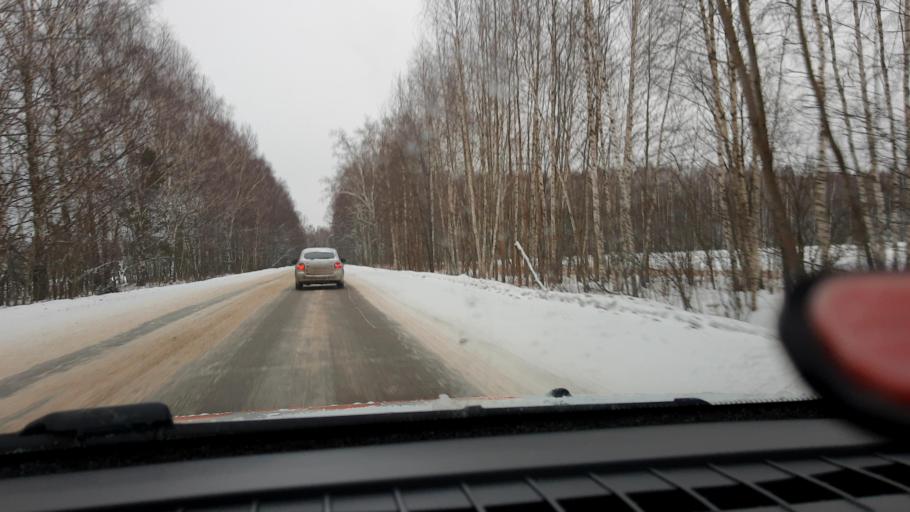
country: RU
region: Nizjnij Novgorod
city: Pamyat' Parizhskoy Kommuny
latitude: 56.2571
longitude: 44.4618
